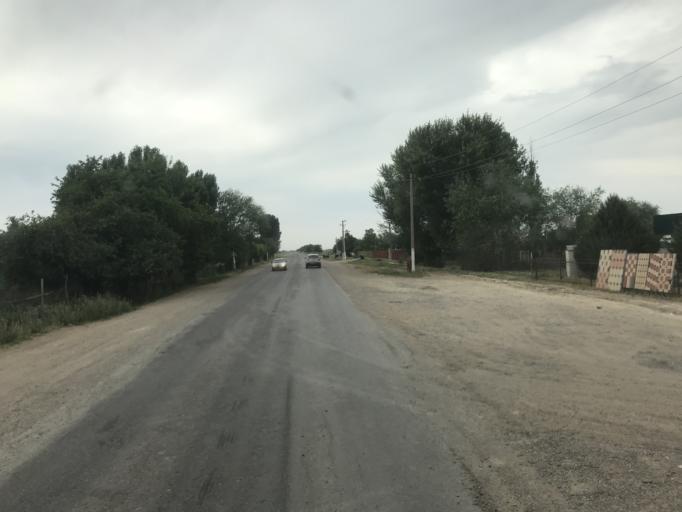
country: KZ
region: Ongtustik Qazaqstan
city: Asykata
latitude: 40.9060
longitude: 68.3538
